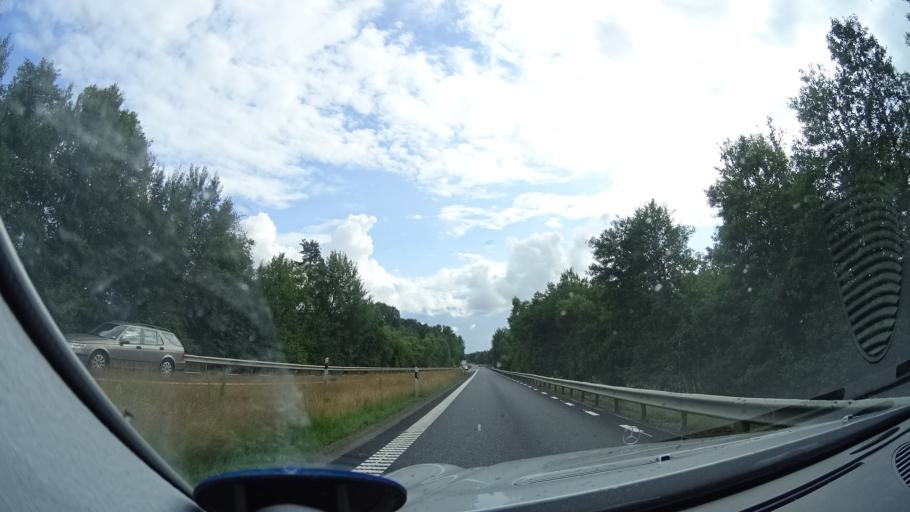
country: SE
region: Blekinge
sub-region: Karlshamns Kommun
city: Svangsta
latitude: 56.2254
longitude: 14.8192
